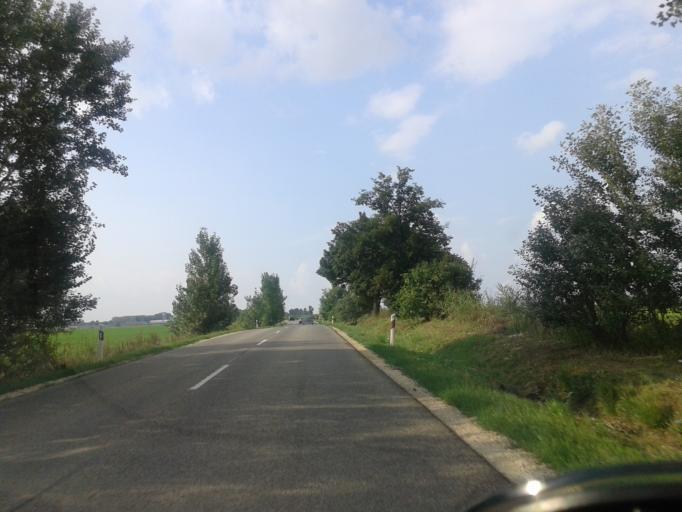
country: HU
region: Pest
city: Domsod
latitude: 47.0584
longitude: 19.0184
